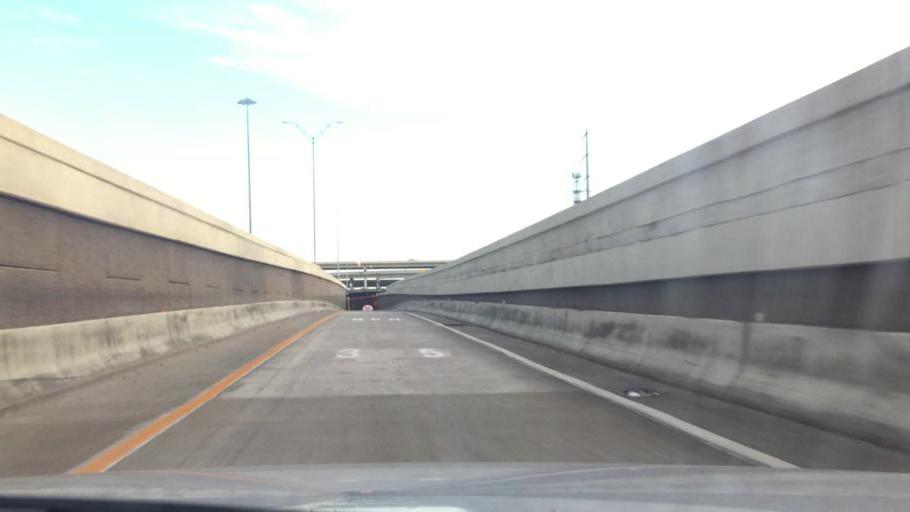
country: US
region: Texas
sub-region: Harris County
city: Bunker Hill Village
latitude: 29.7216
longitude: -95.5575
